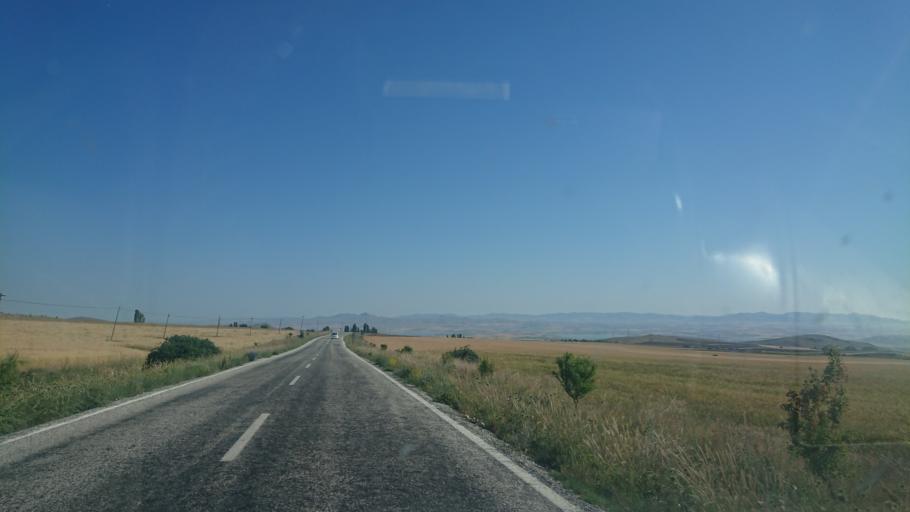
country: TR
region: Aksaray
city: Sariyahsi
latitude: 38.9338
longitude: 33.8333
